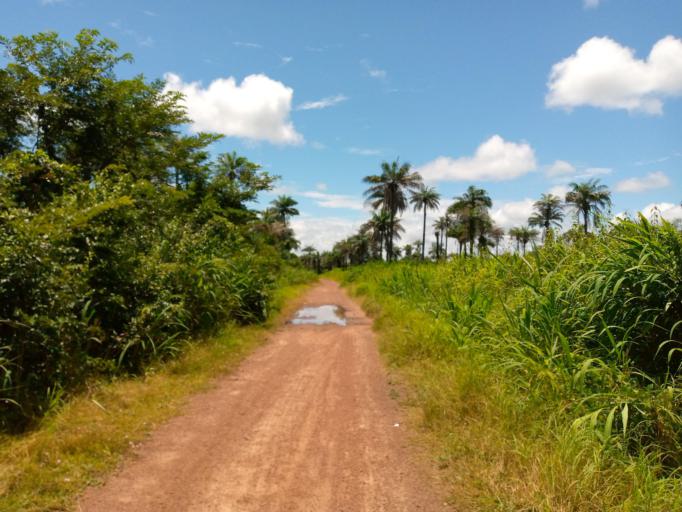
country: SL
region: Northern Province
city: Makeni
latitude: 9.0526
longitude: -12.1542
